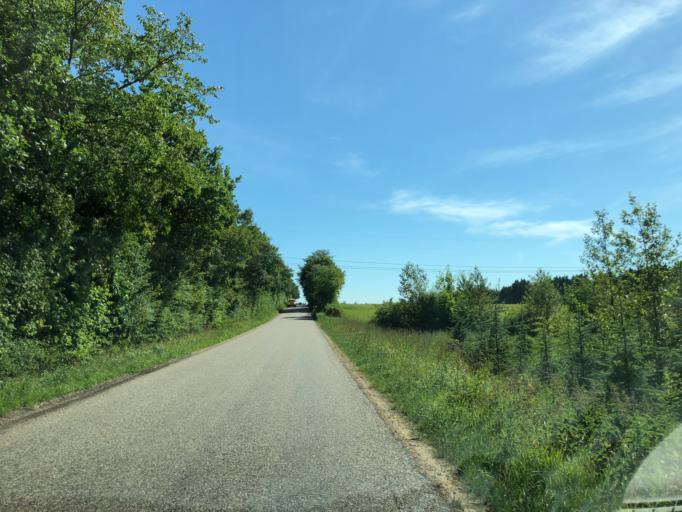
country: DK
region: Central Jutland
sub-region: Holstebro Kommune
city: Vinderup
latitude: 56.4040
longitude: 8.9082
